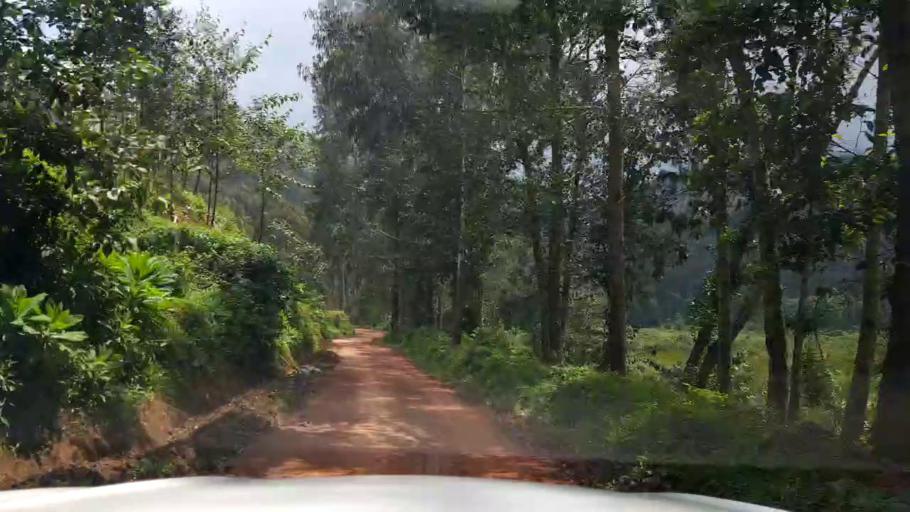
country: UG
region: Western Region
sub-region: Kabale District
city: Kabale
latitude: -1.4243
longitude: 29.8645
